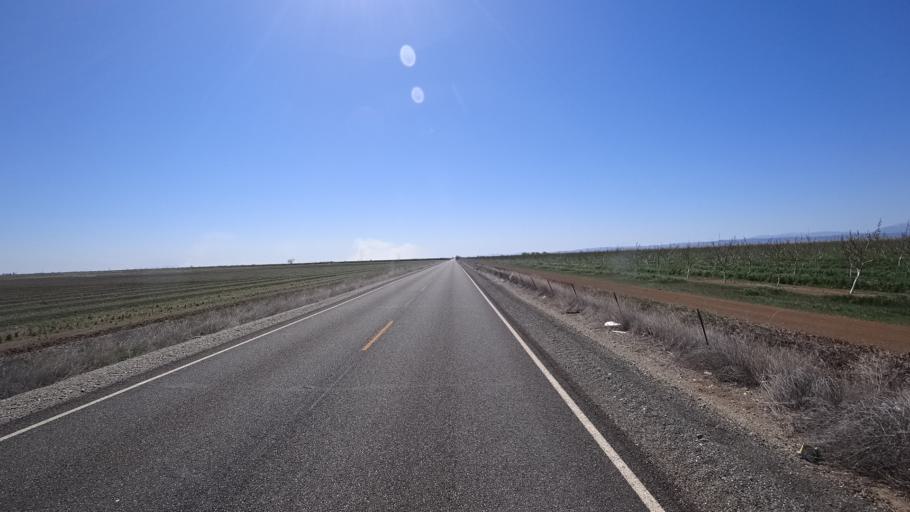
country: US
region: California
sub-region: Glenn County
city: Willows
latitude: 39.5890
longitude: -122.2497
